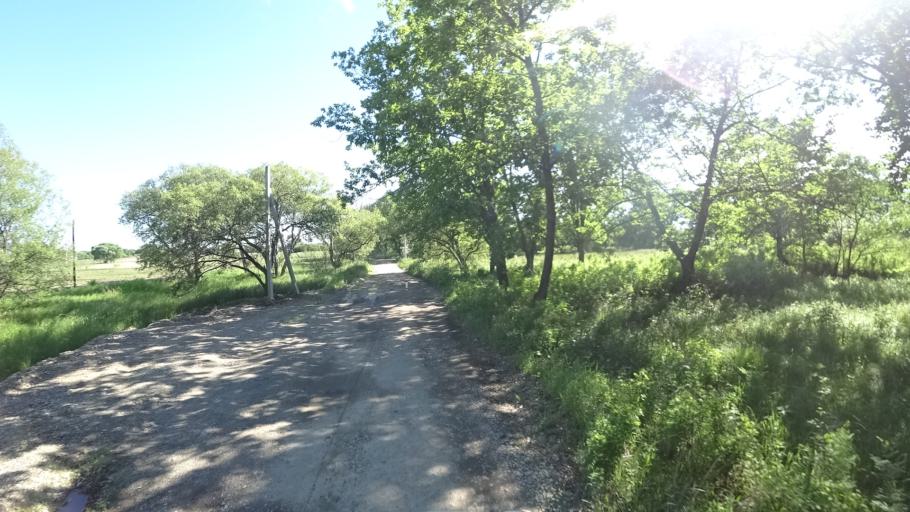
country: RU
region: Khabarovsk Krai
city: Khor
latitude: 47.8879
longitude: 135.0200
